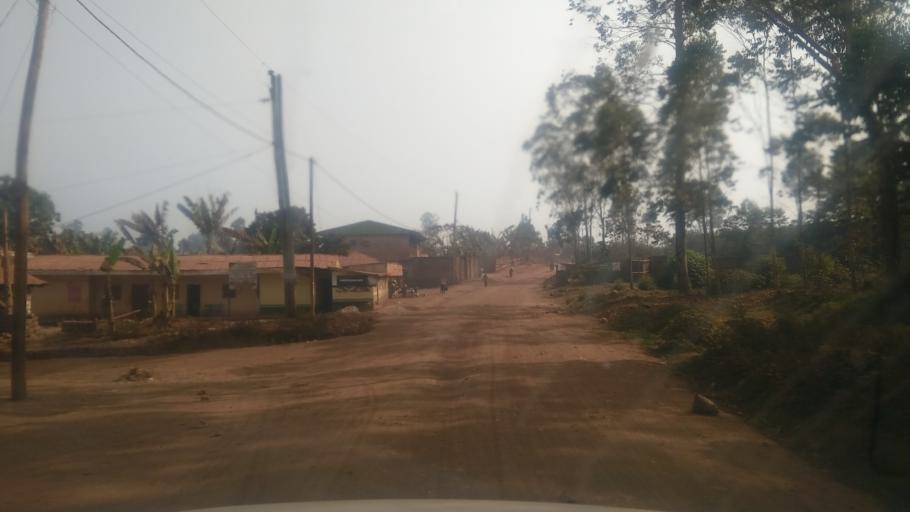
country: CM
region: West
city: Bafoussam
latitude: 5.5135
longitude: 10.4063
